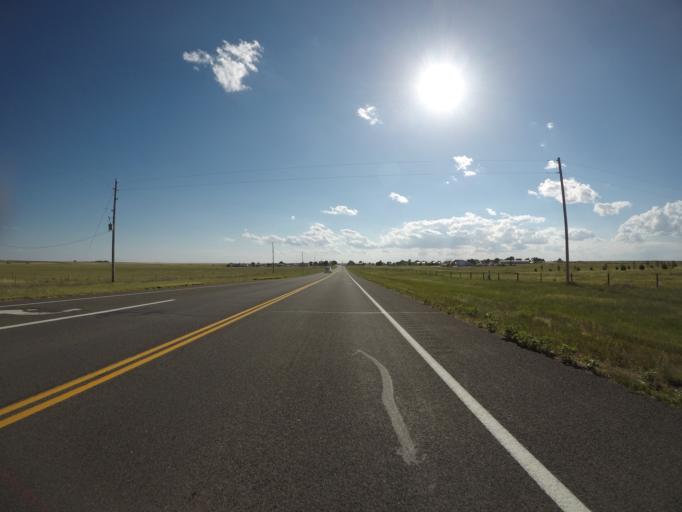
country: US
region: Colorado
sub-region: Morgan County
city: Fort Morgan
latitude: 40.6091
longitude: -103.8332
